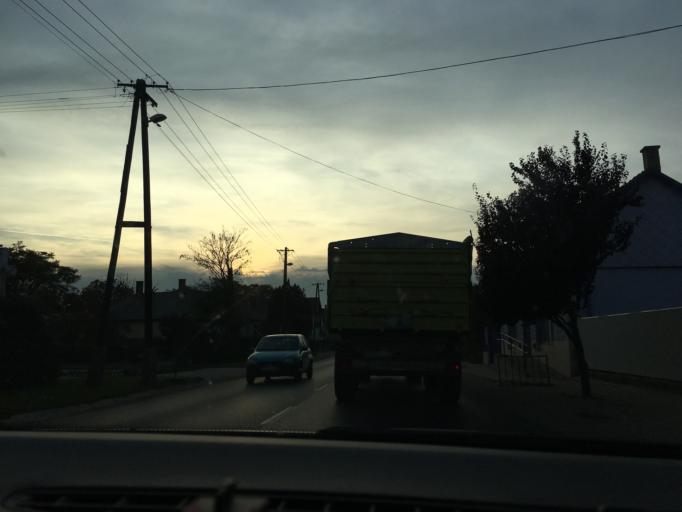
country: HU
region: Szabolcs-Szatmar-Bereg
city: Kallosemjen
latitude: 47.8590
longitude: 21.9291
